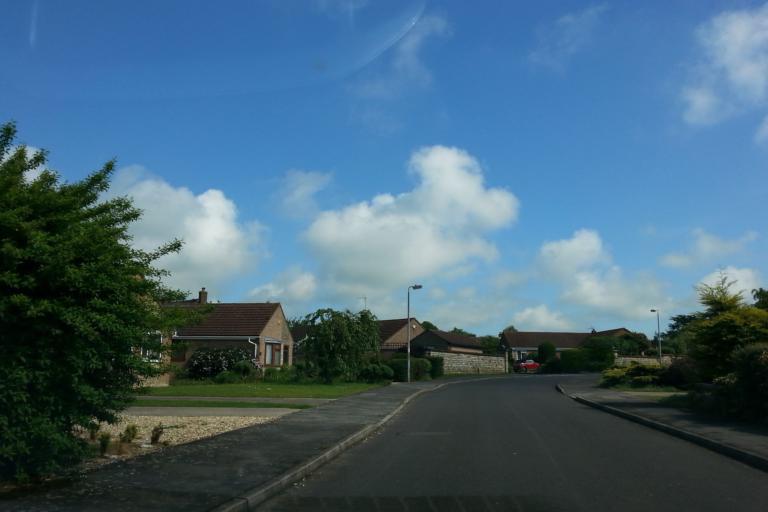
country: GB
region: England
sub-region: District of Rutland
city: Greetham
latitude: 52.8037
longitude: -0.6186
